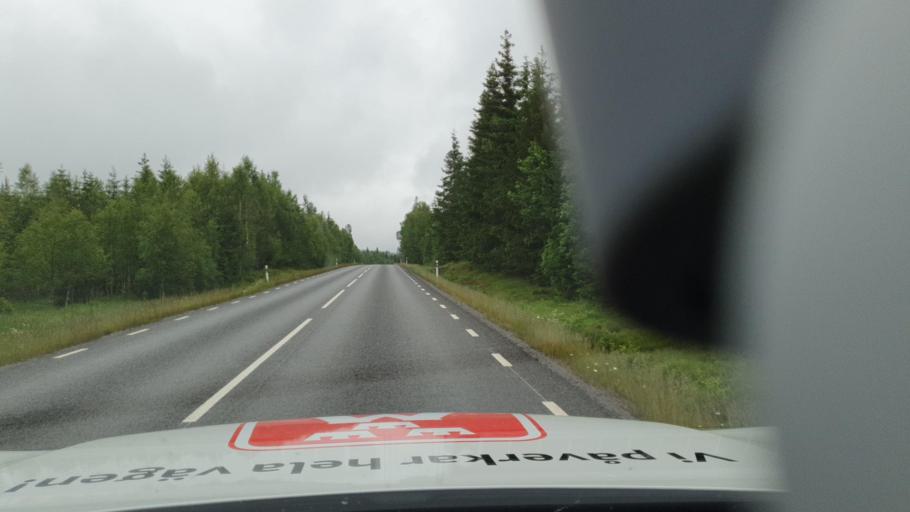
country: SE
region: OErebro
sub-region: Degerfors Kommun
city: Degerfors
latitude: 59.2225
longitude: 14.3543
